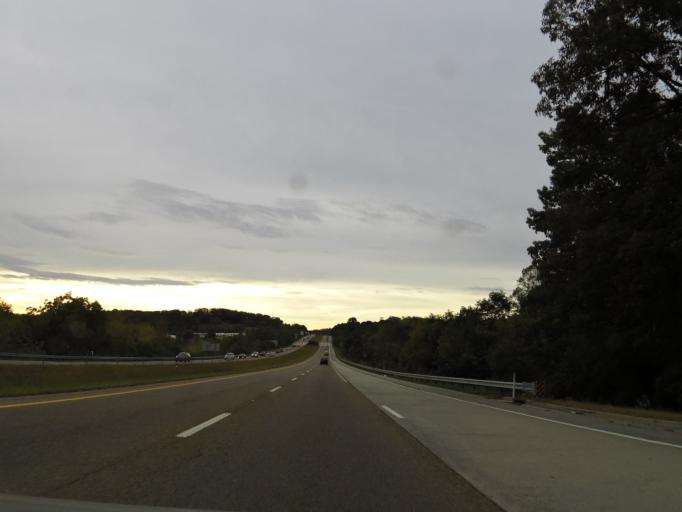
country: US
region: Tennessee
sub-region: Blount County
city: Alcoa
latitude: 35.8389
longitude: -83.9771
